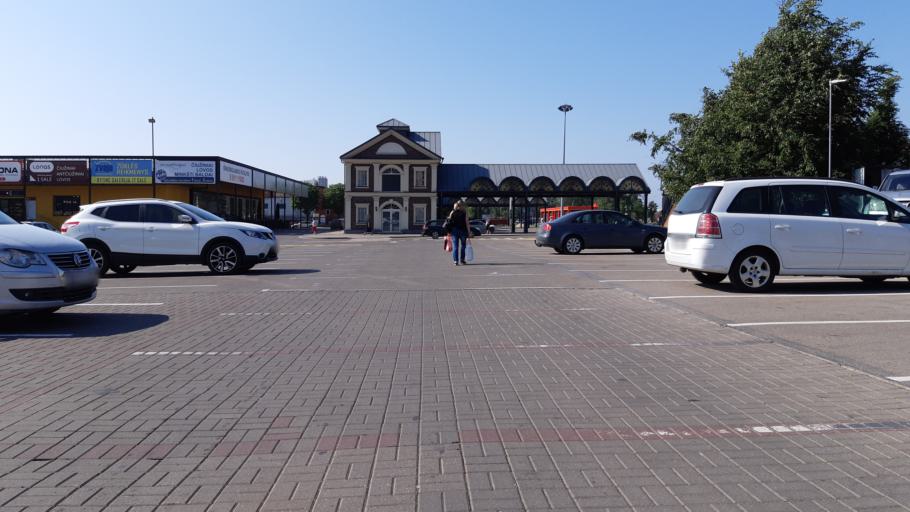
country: LT
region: Kauno apskritis
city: Dainava (Kaunas)
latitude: 54.9163
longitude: 23.9871
